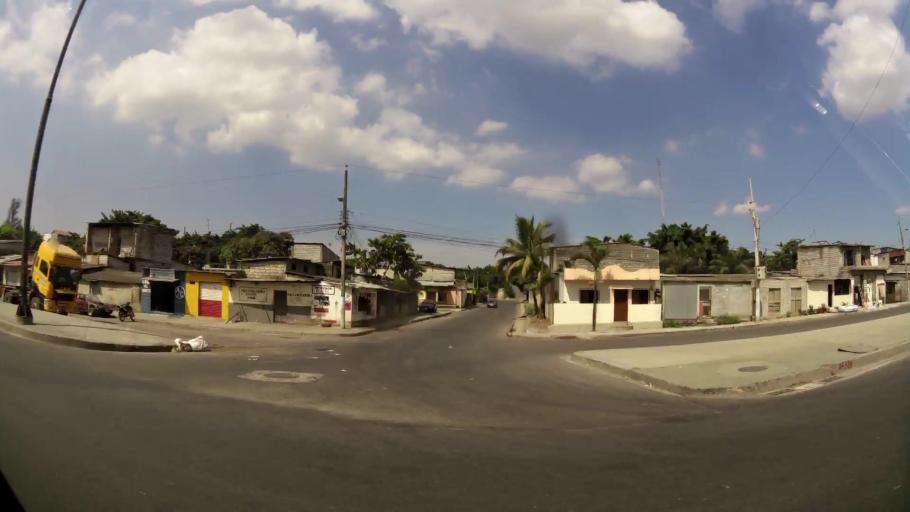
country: EC
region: Guayas
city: Santa Lucia
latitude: -2.1230
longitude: -79.9491
